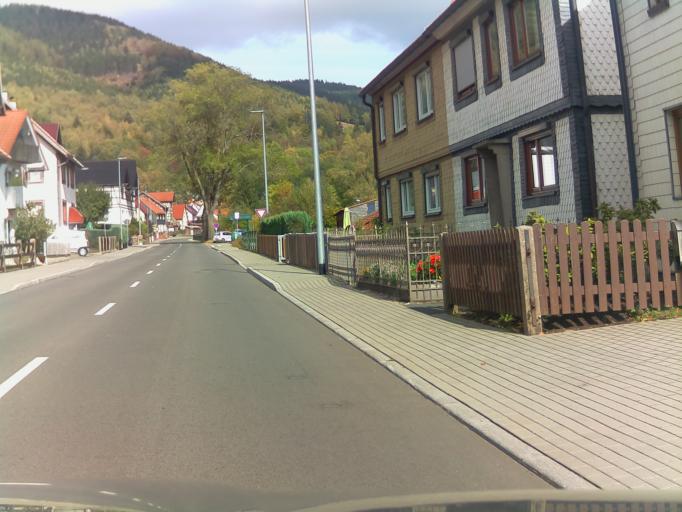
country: DE
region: Thuringia
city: Steinbach-Hallenberg
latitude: 50.7093
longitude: 10.5708
